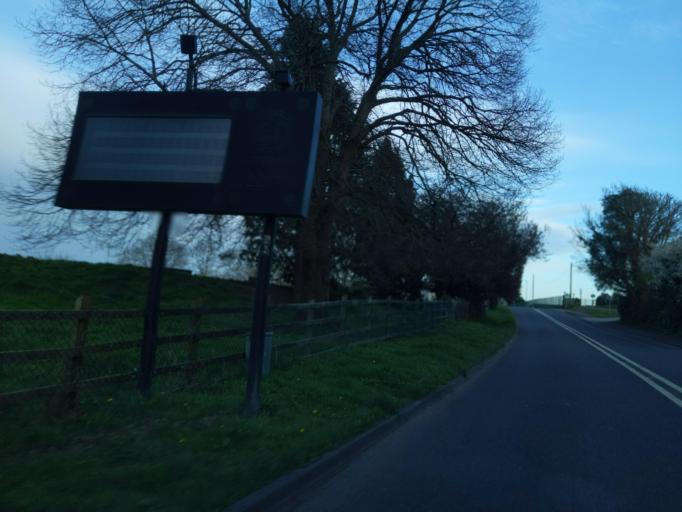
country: GB
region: England
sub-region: Cornwall
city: Torpoint
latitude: 50.3797
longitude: -4.2082
